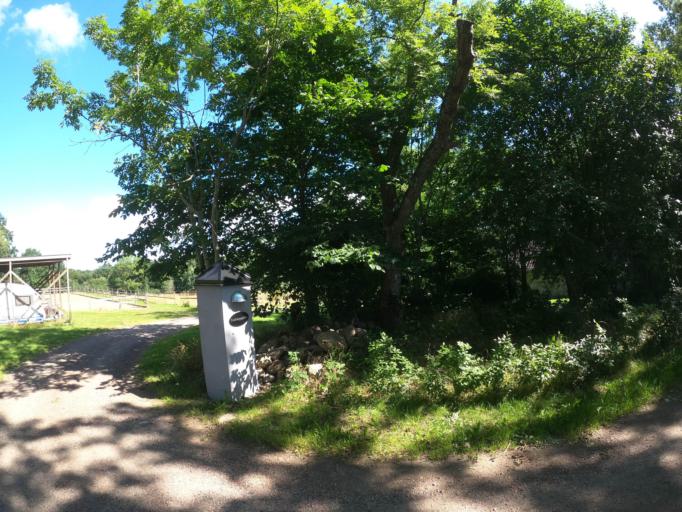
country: SE
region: Skane
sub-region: Lunds Kommun
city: Genarp
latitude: 55.6836
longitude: 13.3916
